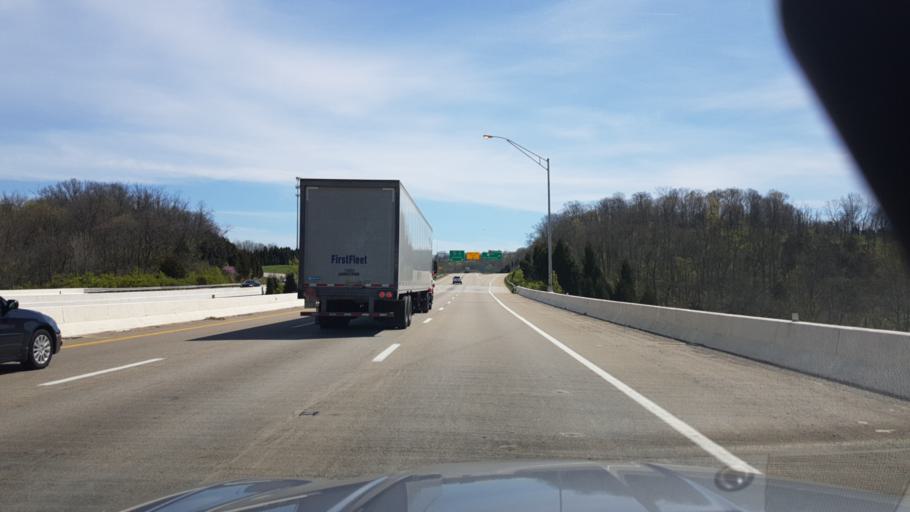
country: US
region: Kentucky
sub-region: Campbell County
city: Silver Grove
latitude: 39.0549
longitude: -84.4010
